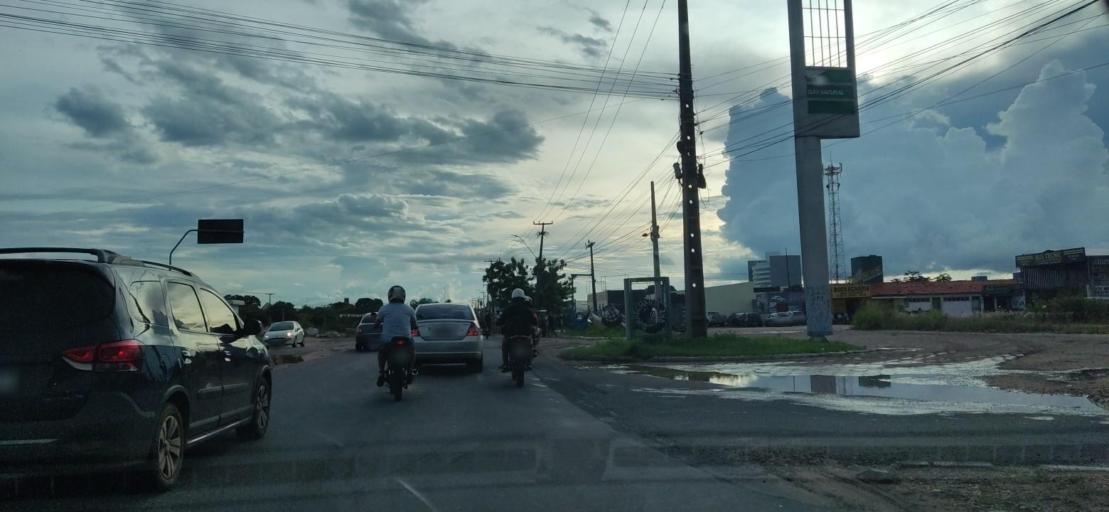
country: BR
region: Piaui
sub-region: Teresina
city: Teresina
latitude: -5.1200
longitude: -42.7895
